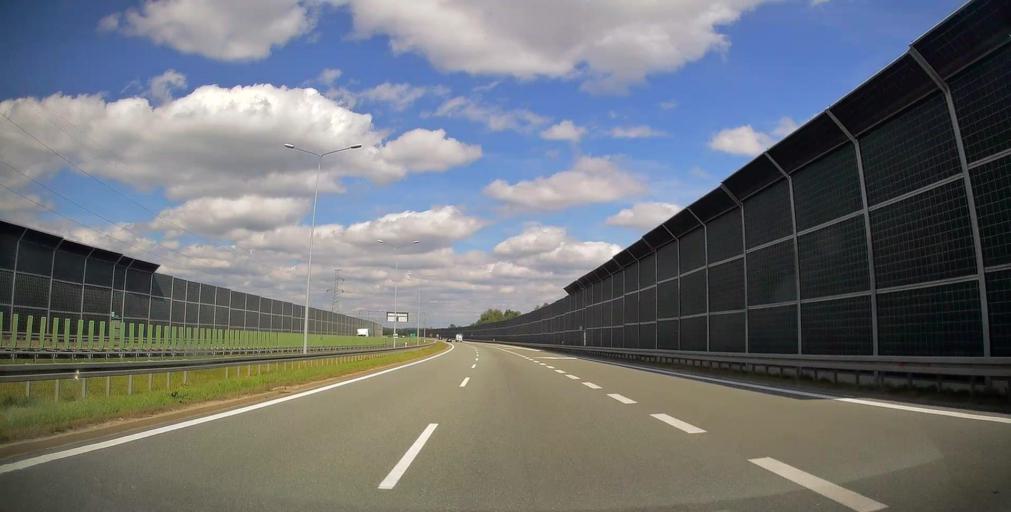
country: PL
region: Swietokrzyskie
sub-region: Powiat kielecki
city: Piekoszow
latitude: 50.8591
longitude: 20.5102
